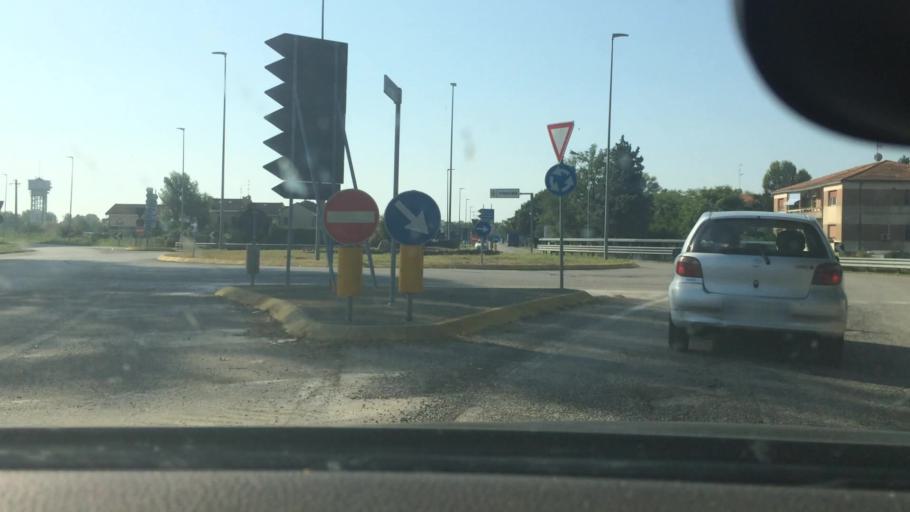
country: IT
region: Emilia-Romagna
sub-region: Provincia di Ferrara
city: Comacchio
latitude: 44.7037
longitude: 12.1650
